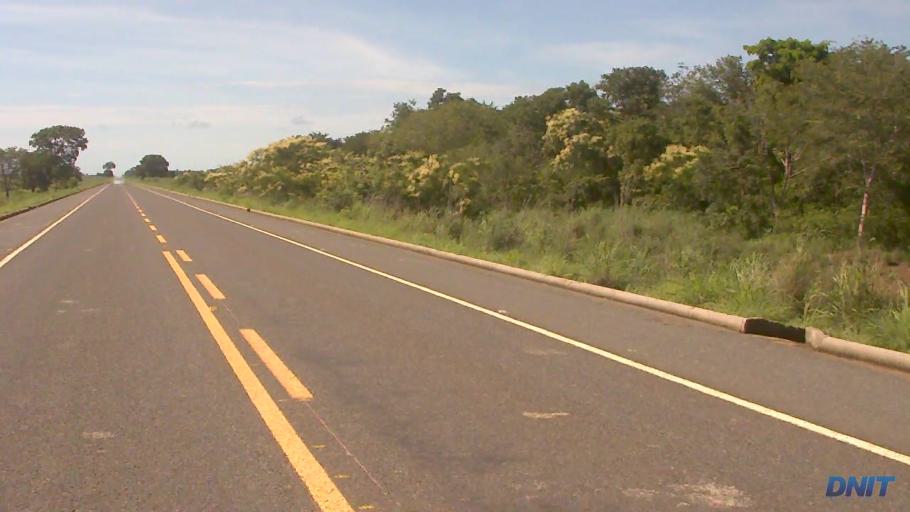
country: BR
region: Goias
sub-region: Sao Miguel Do Araguaia
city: Sao Miguel do Araguaia
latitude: -13.4121
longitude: -50.1318
